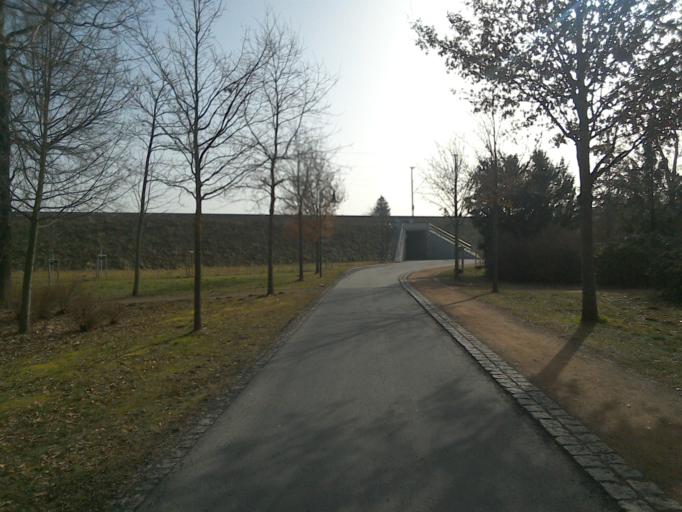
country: DE
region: Saxony
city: Grossenhain
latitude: 51.2901
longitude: 13.5187
